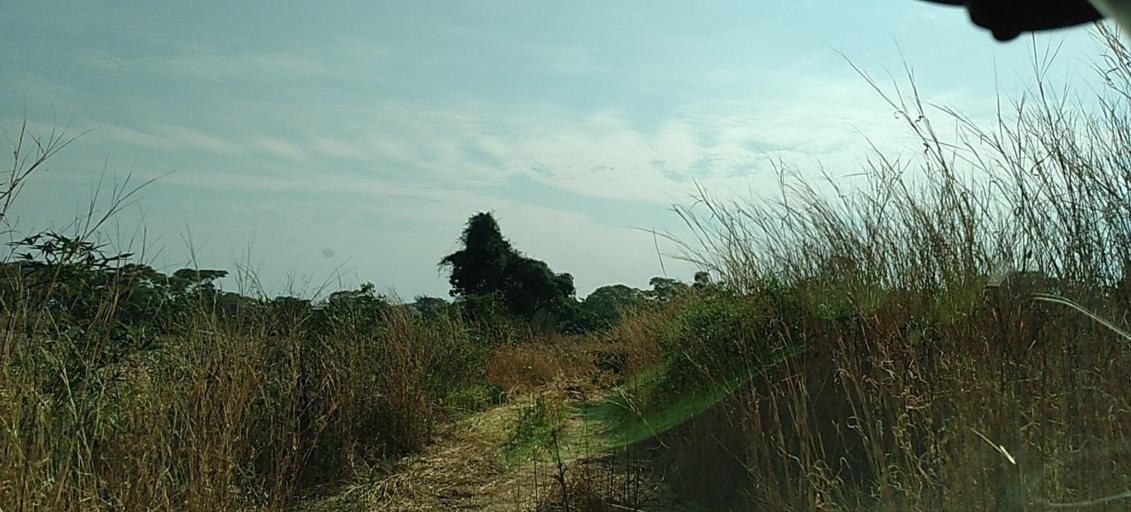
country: ZM
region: North-Western
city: Kalengwa
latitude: -13.2371
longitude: 25.0563
